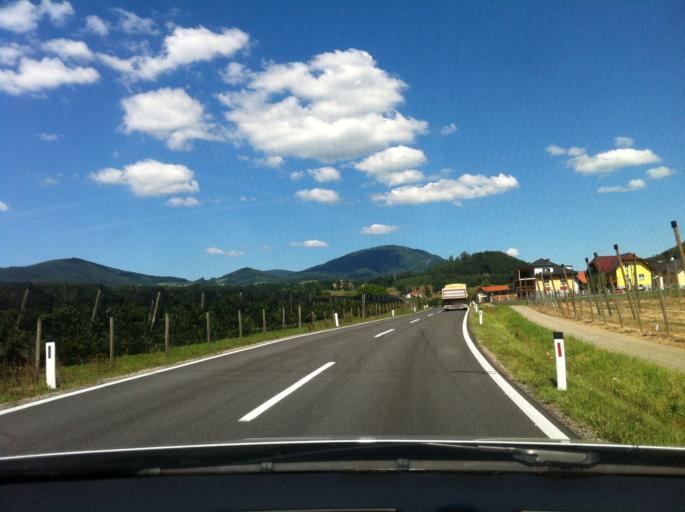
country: AT
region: Styria
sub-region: Politischer Bezirk Weiz
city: Floing
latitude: 47.2435
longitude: 15.7361
